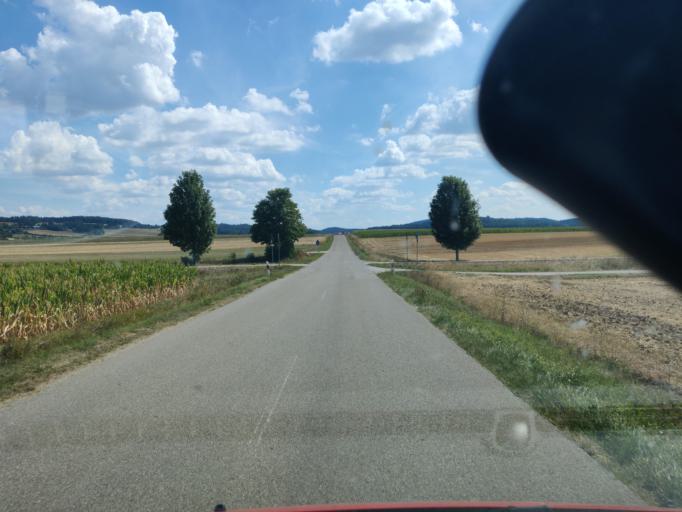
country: DE
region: Bavaria
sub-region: Regierungsbezirk Mittelfranken
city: Thalmassing
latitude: 49.1066
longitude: 11.1954
